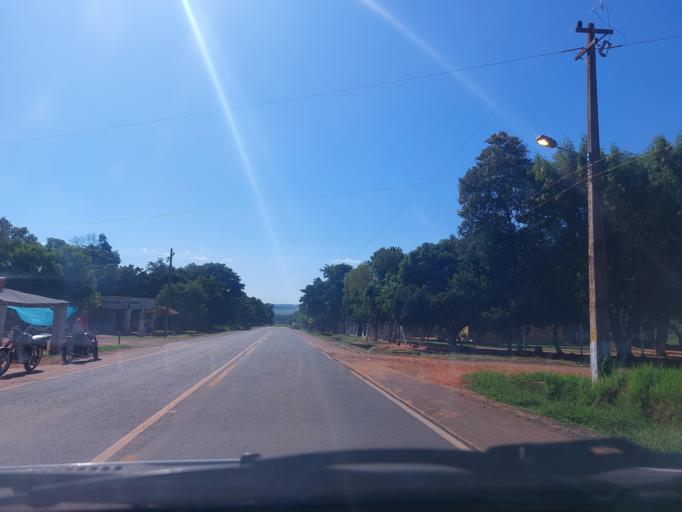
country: PY
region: San Pedro
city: Guayaybi
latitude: -24.3148
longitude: -56.1597
